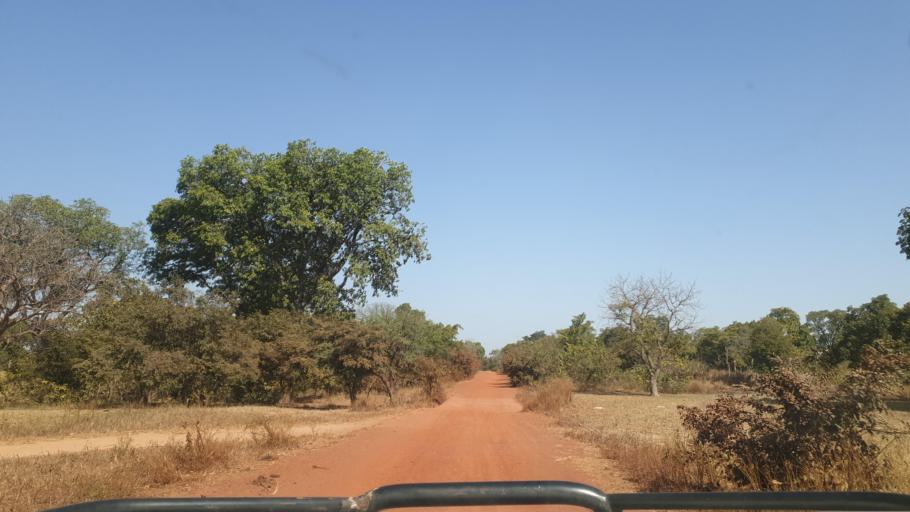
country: ML
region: Sikasso
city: Bougouni
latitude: 11.8393
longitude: -6.9783
